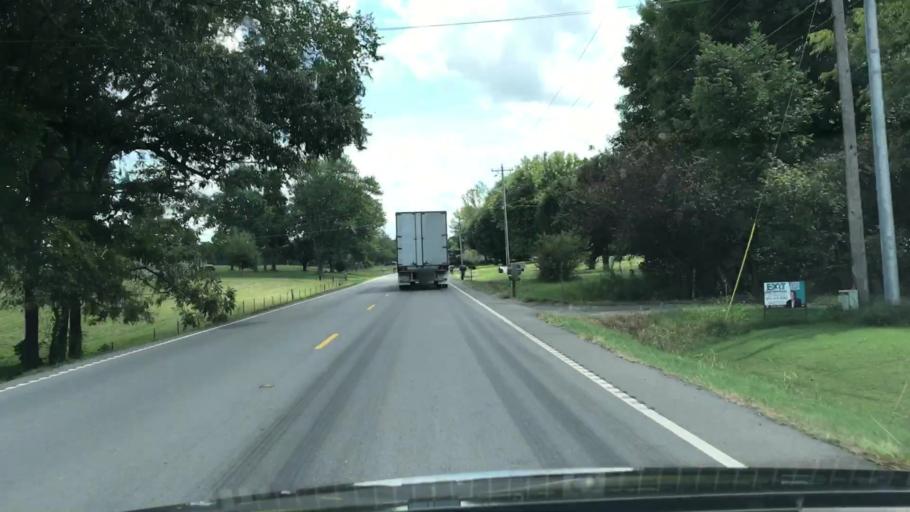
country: US
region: Tennessee
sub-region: Robertson County
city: Cross Plains
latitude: 36.5364
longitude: -86.6575
